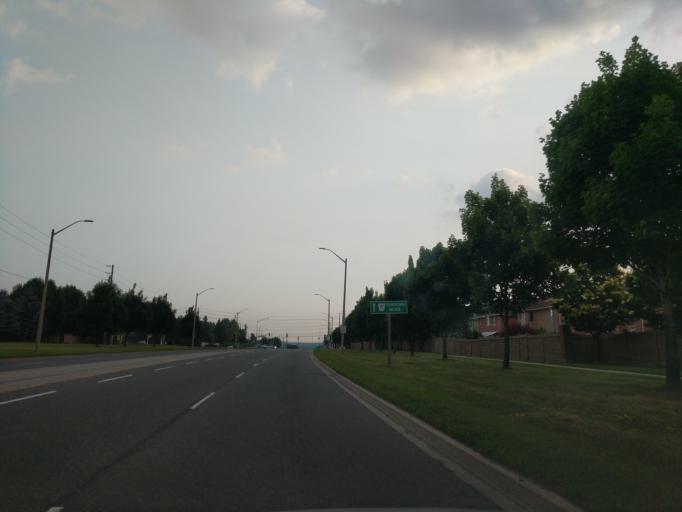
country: CA
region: Ontario
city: Markham
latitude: 43.8472
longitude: -79.2793
